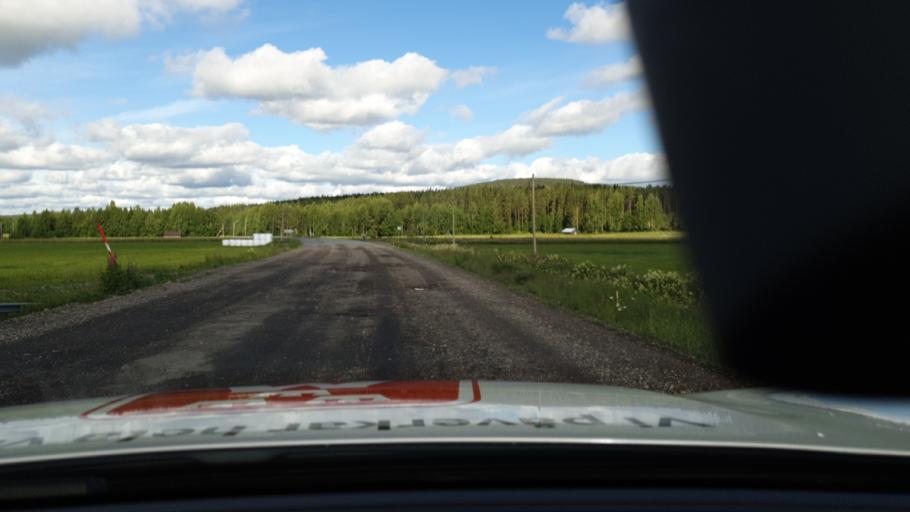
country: SE
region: Norrbotten
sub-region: Bodens Kommun
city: Boden
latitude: 65.8579
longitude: 21.4661
